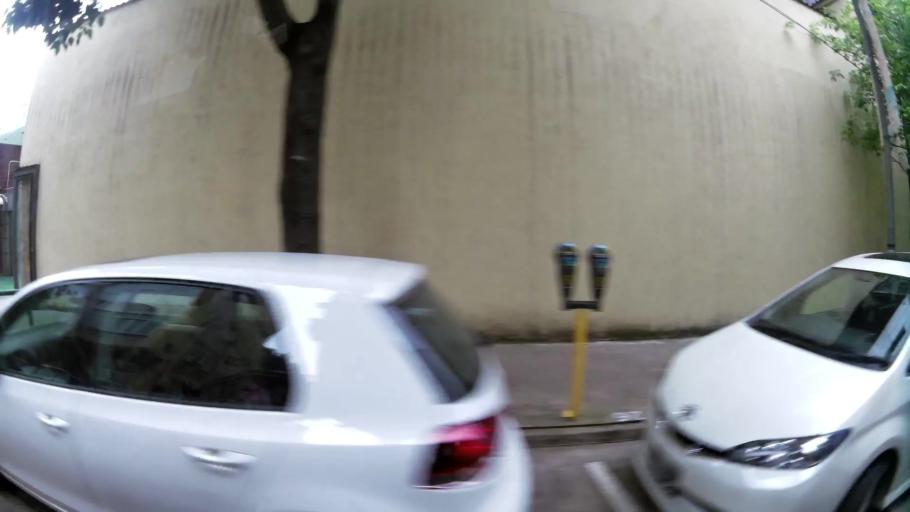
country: MO
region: Macau
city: Macau
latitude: 22.1936
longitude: 113.5452
